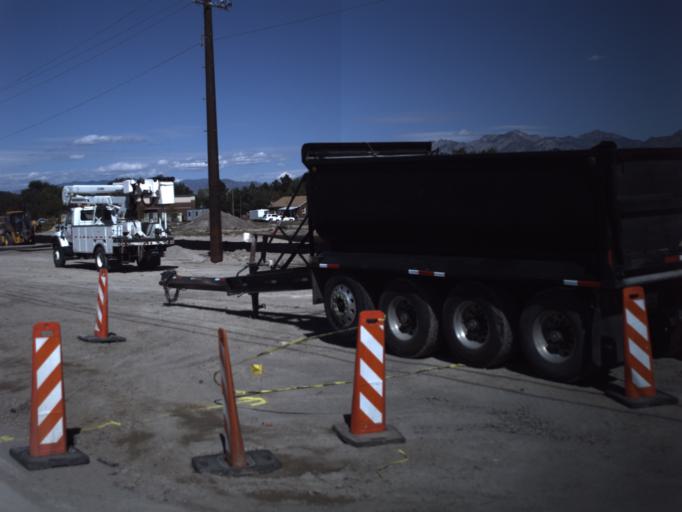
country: US
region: Utah
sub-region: Salt Lake County
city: Riverton
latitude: 40.5193
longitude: -111.9387
